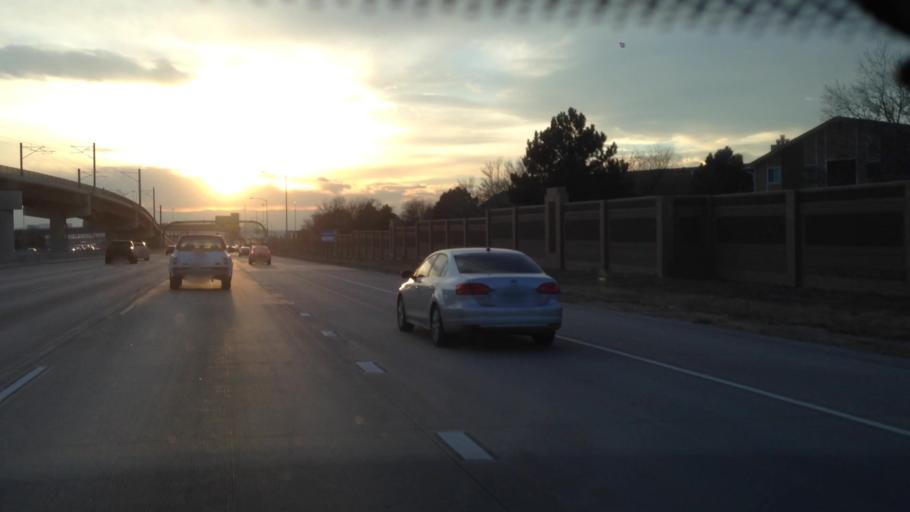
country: US
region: Colorado
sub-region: Adams County
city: Aurora
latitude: 39.6625
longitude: -104.8360
